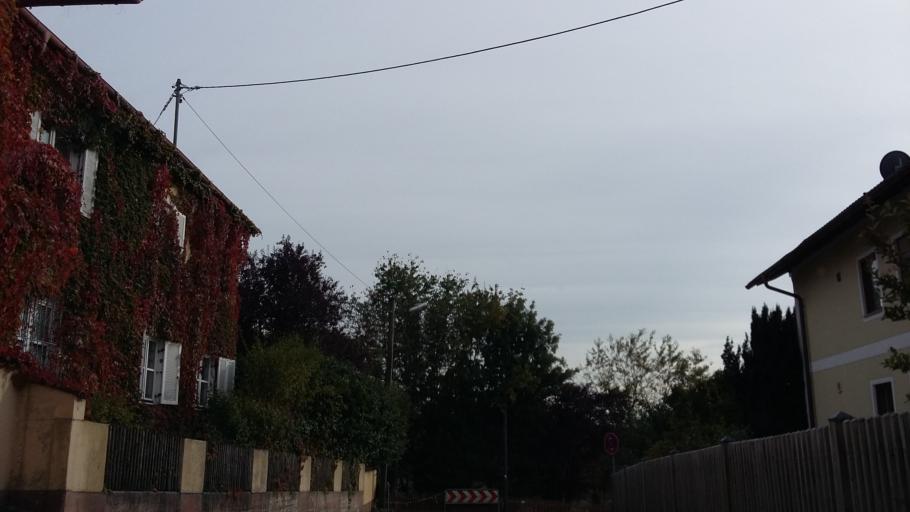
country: DE
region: Bavaria
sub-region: Upper Bavaria
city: Munsing
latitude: 47.9043
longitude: 11.3696
